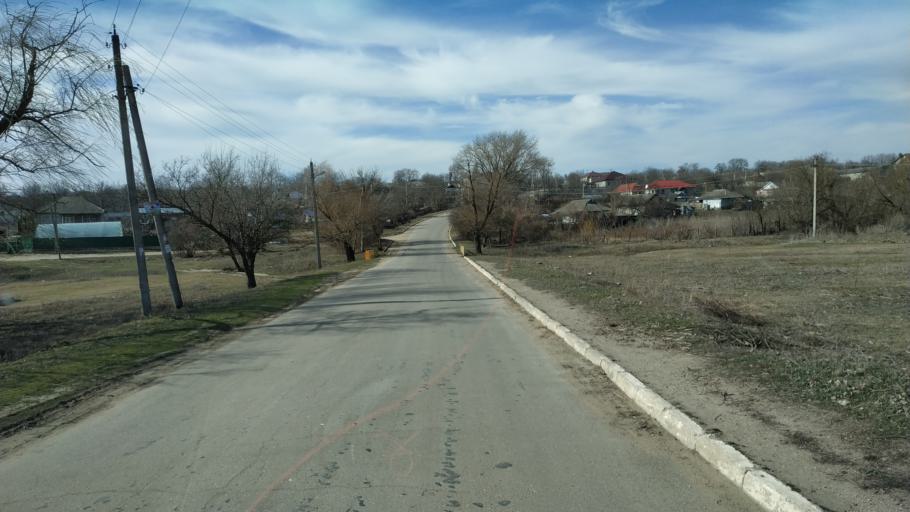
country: MD
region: Nisporeni
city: Nisporeni
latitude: 46.9624
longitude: 28.2164
